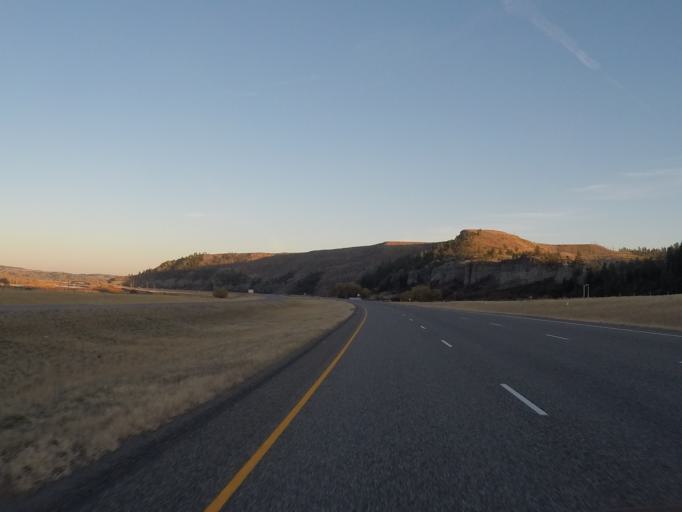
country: US
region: Montana
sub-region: Sweet Grass County
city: Big Timber
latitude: 45.7336
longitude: -109.7539
